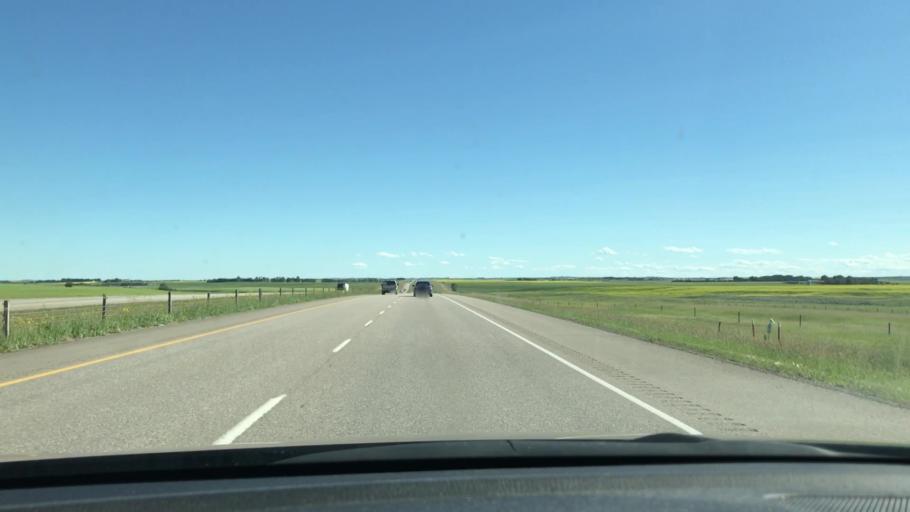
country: CA
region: Alberta
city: Carstairs
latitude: 51.6475
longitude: -114.0257
